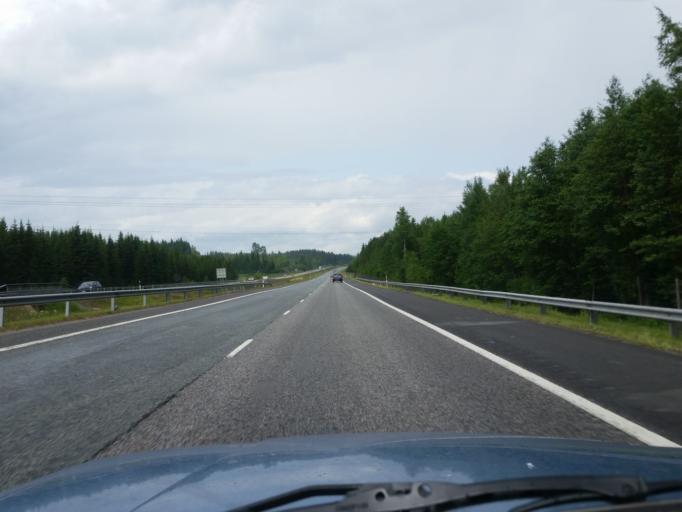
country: FI
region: Paijanne Tavastia
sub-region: Lahti
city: Heinola
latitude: 61.1240
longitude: 25.9364
